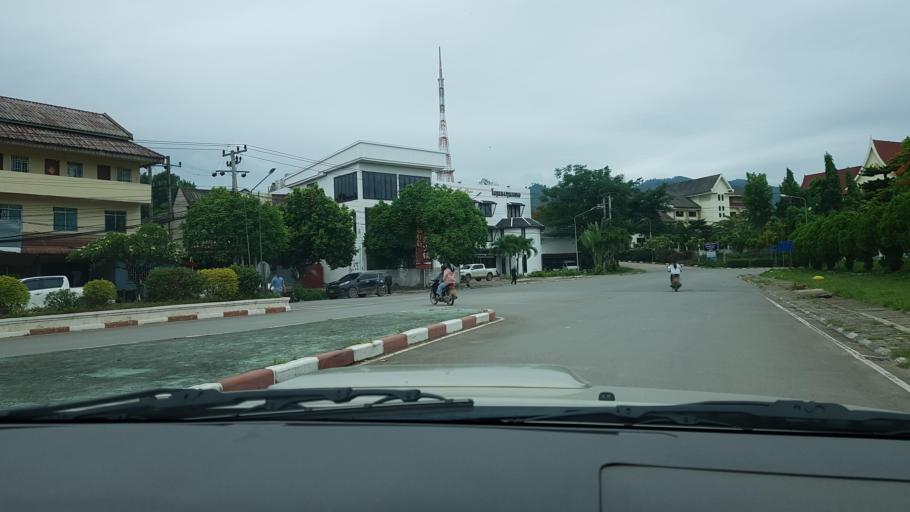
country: LA
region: Oudomxai
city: Muang Xay
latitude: 20.6916
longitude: 101.9826
